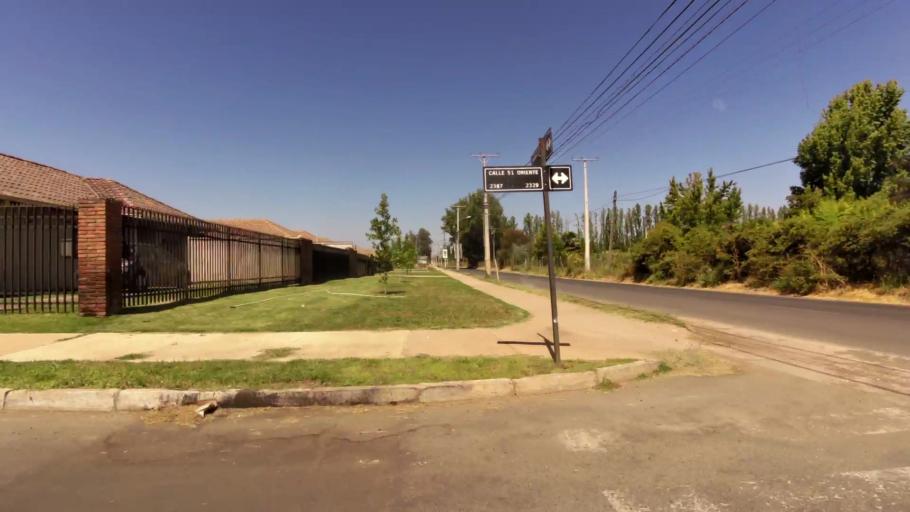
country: CL
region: Maule
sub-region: Provincia de Talca
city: Talca
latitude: -35.4336
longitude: -71.5971
